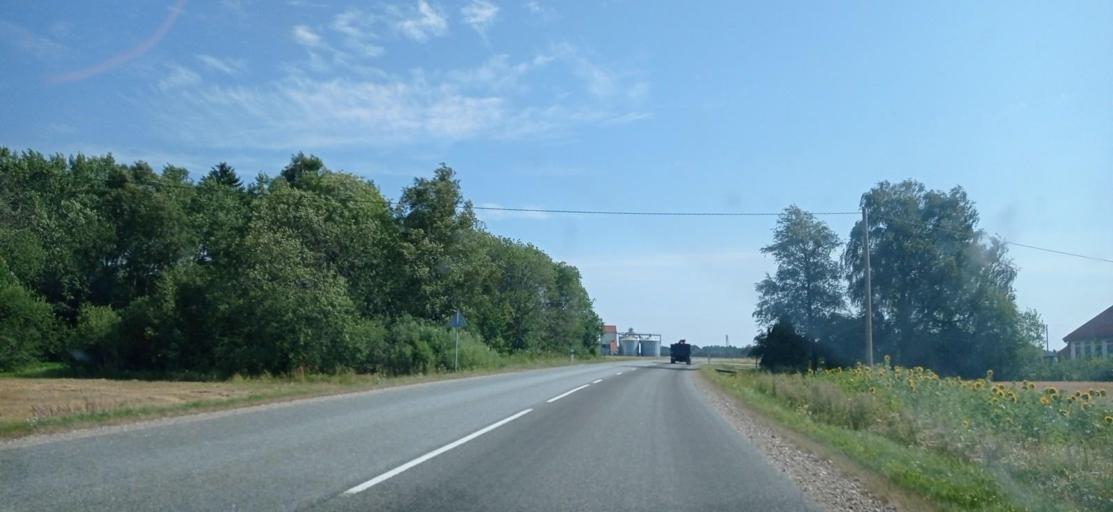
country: LV
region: Ventspils
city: Ventspils
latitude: 57.2303
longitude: 21.4694
